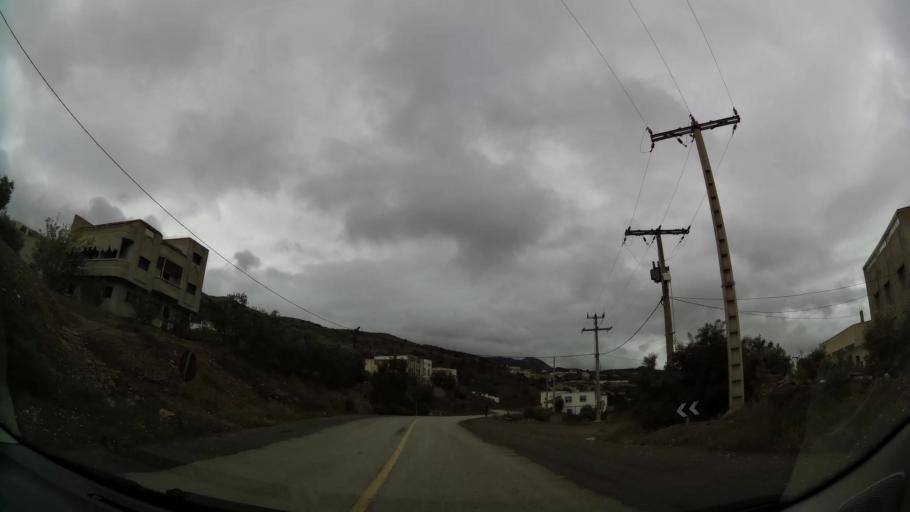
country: MA
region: Taza-Al Hoceima-Taounate
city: Imzourene
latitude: 34.9599
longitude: -3.8111
